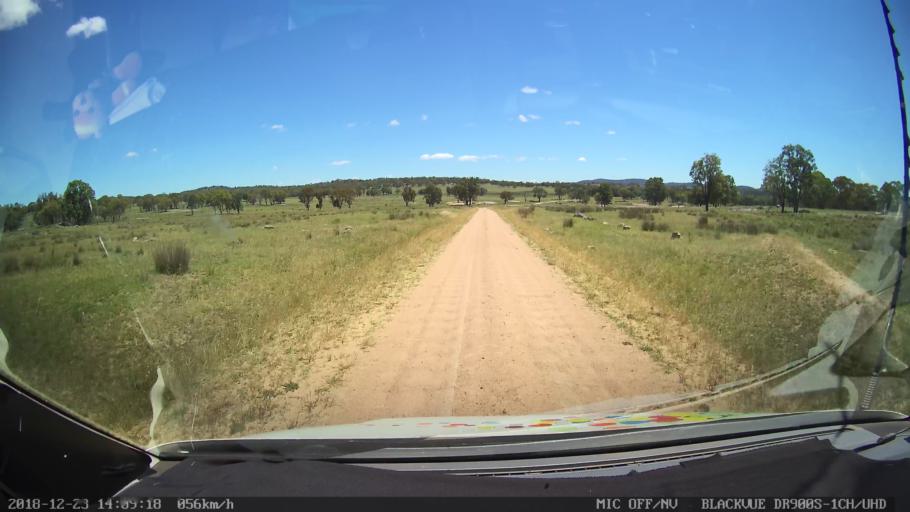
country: AU
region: New South Wales
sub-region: Tamworth Municipality
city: Manilla
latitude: -30.6444
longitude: 151.0630
